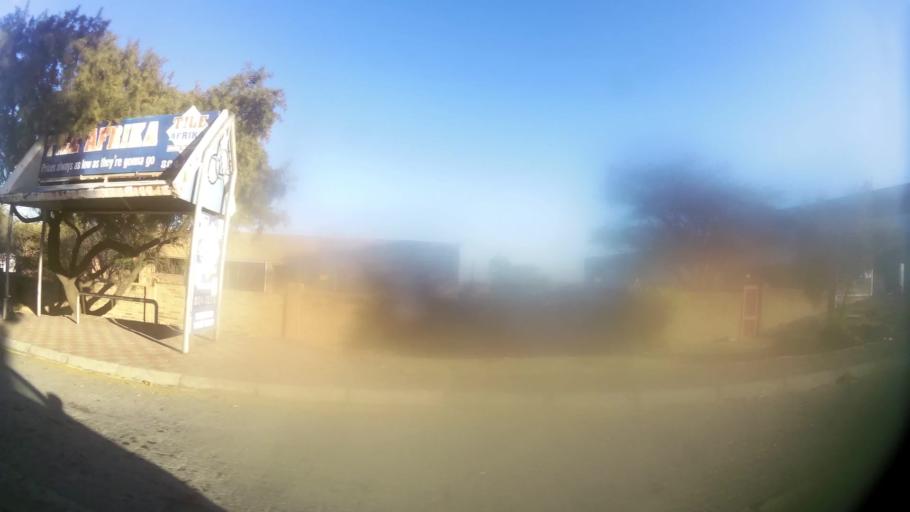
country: ZA
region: Gauteng
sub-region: City of Johannesburg Metropolitan Municipality
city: Midrand
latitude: -26.0145
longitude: 28.1188
